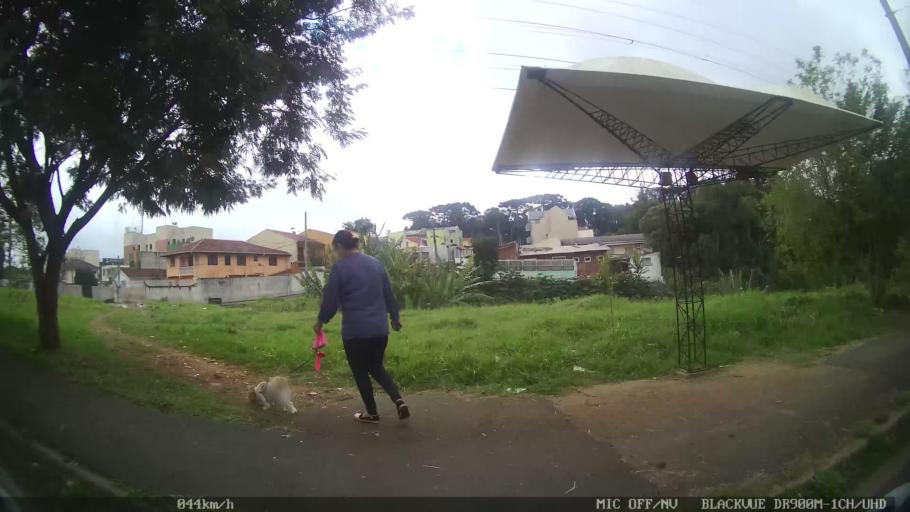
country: BR
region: Parana
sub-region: Curitiba
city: Curitiba
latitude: -25.3746
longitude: -49.2615
